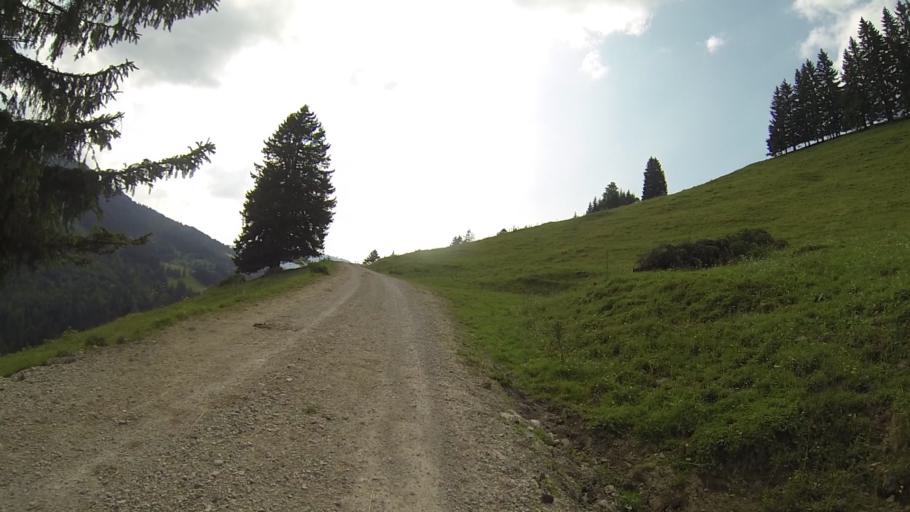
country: AT
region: Tyrol
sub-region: Politischer Bezirk Reutte
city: Jungholz
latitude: 47.5727
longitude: 10.4764
